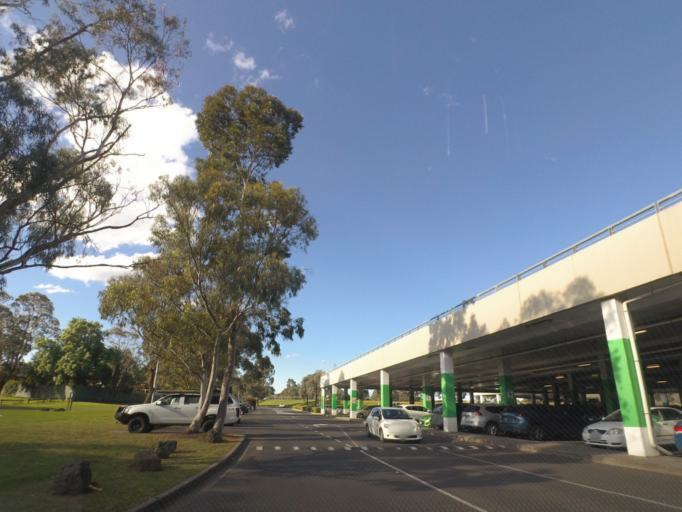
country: AU
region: Victoria
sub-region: Knox
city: Knoxfield
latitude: -37.8677
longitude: 145.2414
